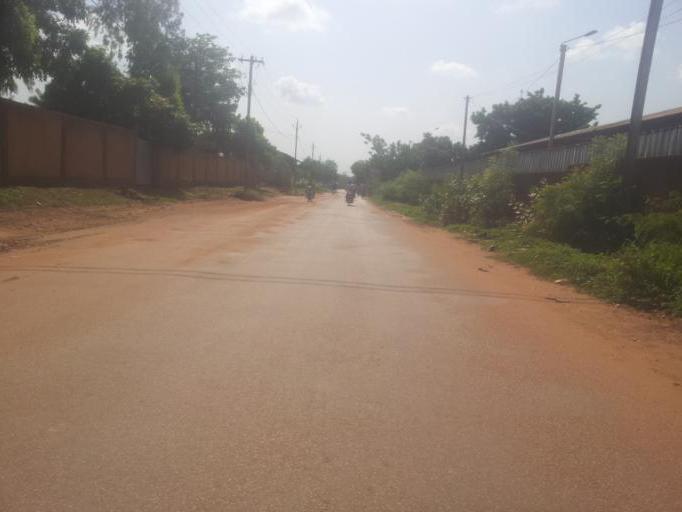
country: BF
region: Centre
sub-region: Kadiogo Province
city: Ouagadougou
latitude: 12.3624
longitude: -1.5425
